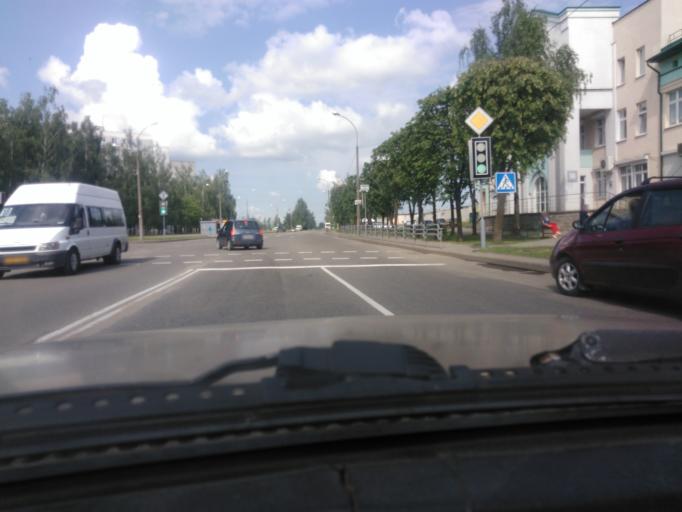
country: BY
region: Mogilev
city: Mahilyow
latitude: 53.9316
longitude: 30.3639
